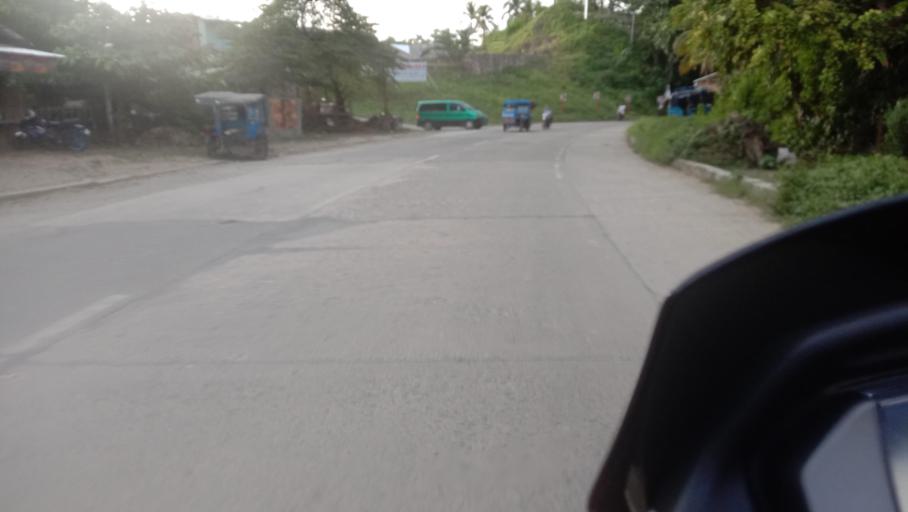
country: PH
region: Caraga
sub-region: Province of Surigao del Sur
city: Barobo
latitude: 8.5283
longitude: 126.1197
